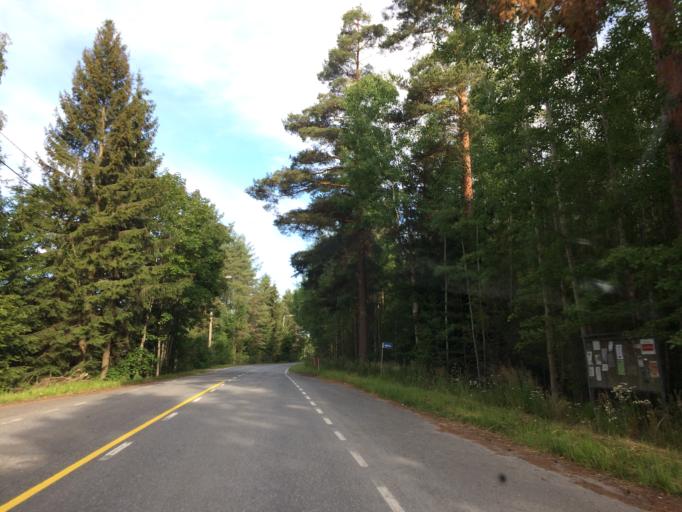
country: FI
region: Haeme
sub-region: Haemeenlinna
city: Janakkala
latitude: 60.9290
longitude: 24.5765
